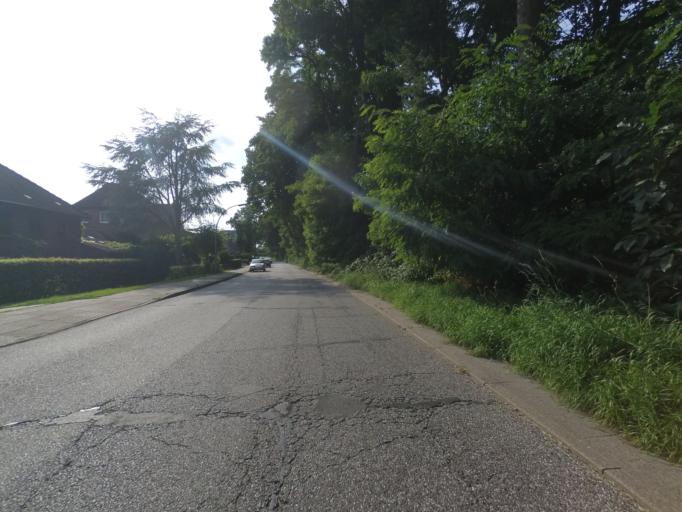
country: DE
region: Hamburg
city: Bergedorf
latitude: 53.4867
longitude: 10.1889
